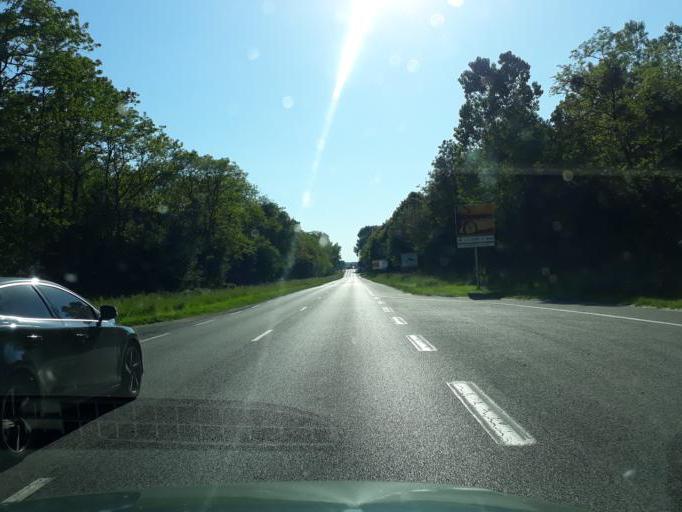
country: FR
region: Bourgogne
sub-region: Departement de la Nievre
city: Cosne-Cours-sur-Loire
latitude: 47.4114
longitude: 2.9156
